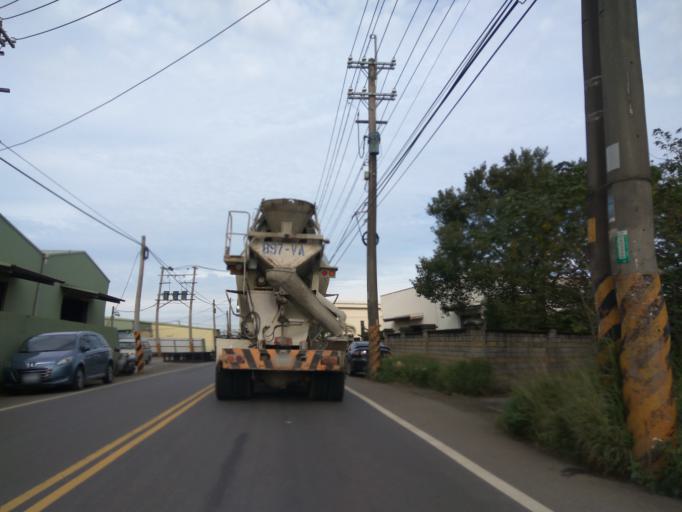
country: TW
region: Taiwan
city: Daxi
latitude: 24.9406
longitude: 121.1589
